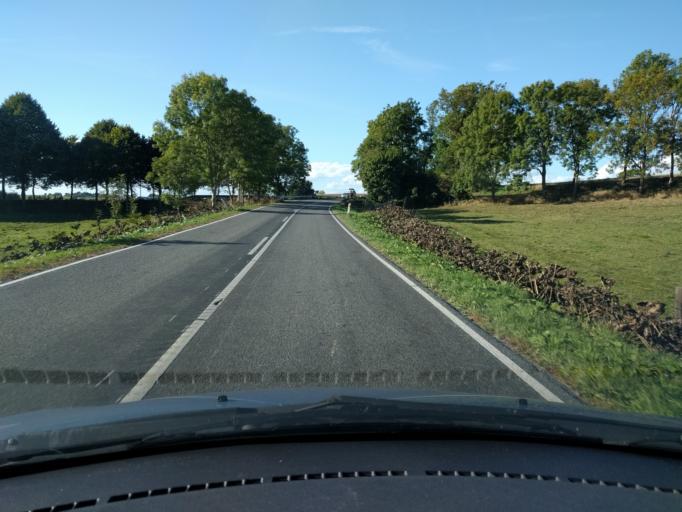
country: DK
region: South Denmark
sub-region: Assens Kommune
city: Assens
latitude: 55.2286
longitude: 9.9901
